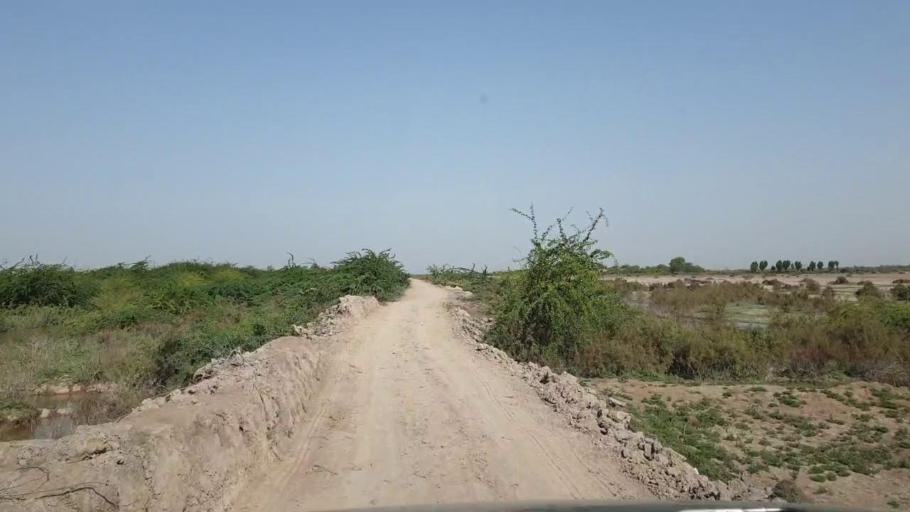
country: PK
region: Sindh
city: Tando Bago
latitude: 24.6458
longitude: 69.0719
